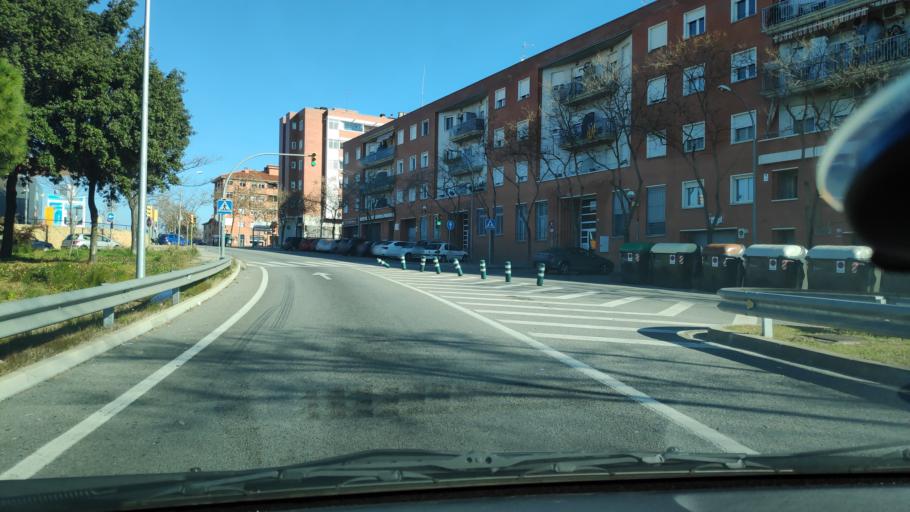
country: ES
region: Catalonia
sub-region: Provincia de Barcelona
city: Sant Quirze del Valles
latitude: 41.5717
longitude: 2.0798
